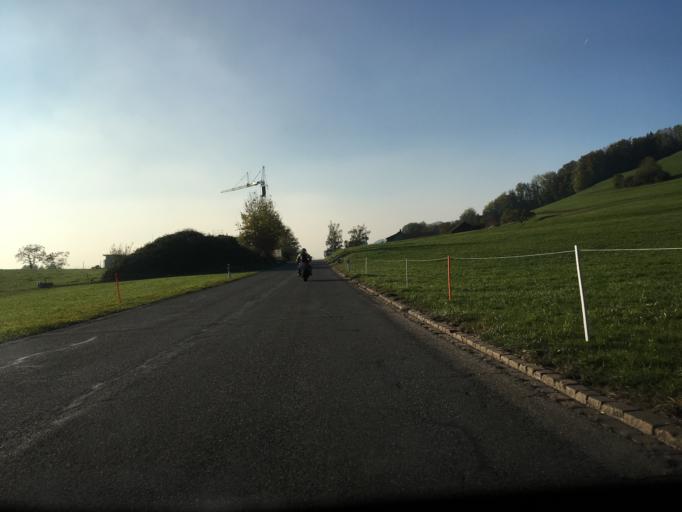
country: CH
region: Zurich
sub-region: Bezirk Hinwil
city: Baretswil
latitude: 47.3328
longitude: 8.8703
